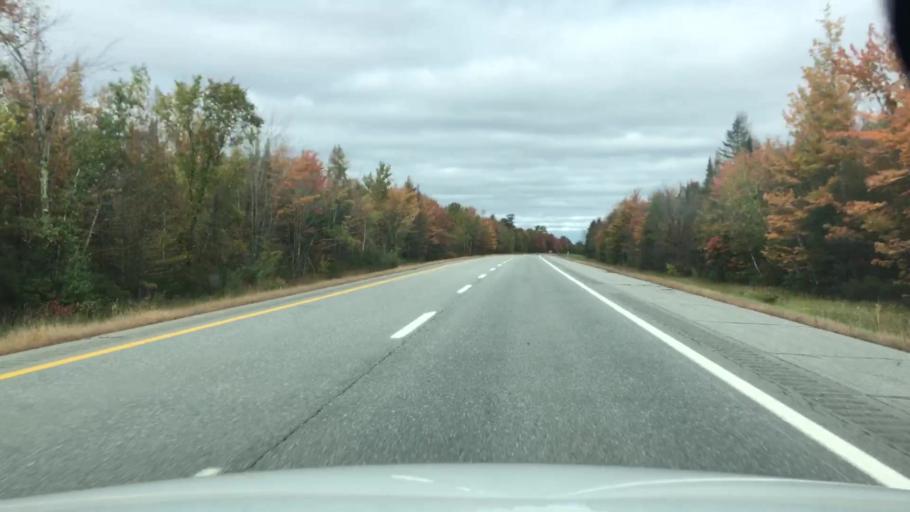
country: US
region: Maine
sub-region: Waldo County
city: Burnham
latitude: 44.6905
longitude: -69.4703
